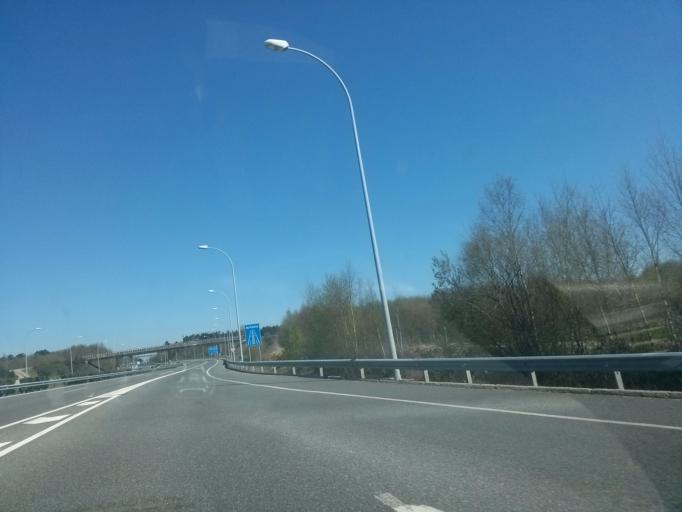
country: ES
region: Galicia
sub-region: Provincia de Lugo
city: Lugo
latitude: 43.0160
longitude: -7.5194
